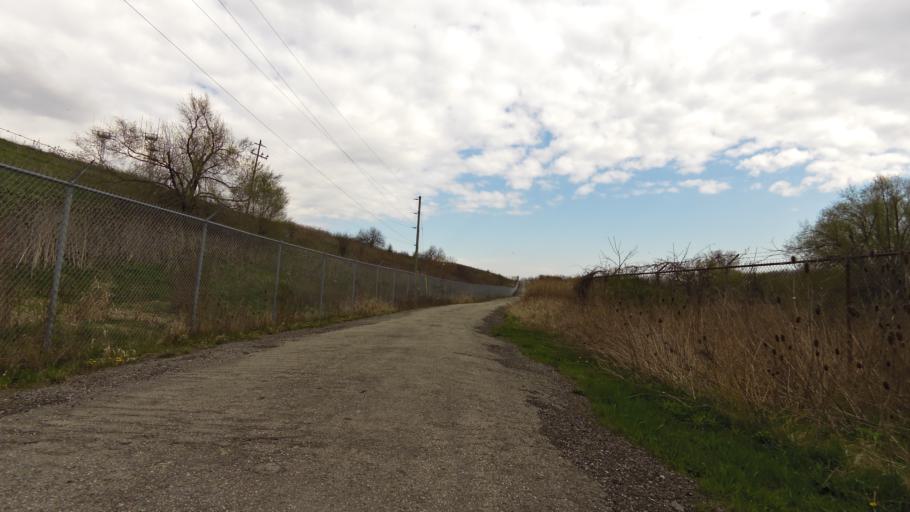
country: CA
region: Ontario
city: Etobicoke
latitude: 43.6641
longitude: -79.6319
